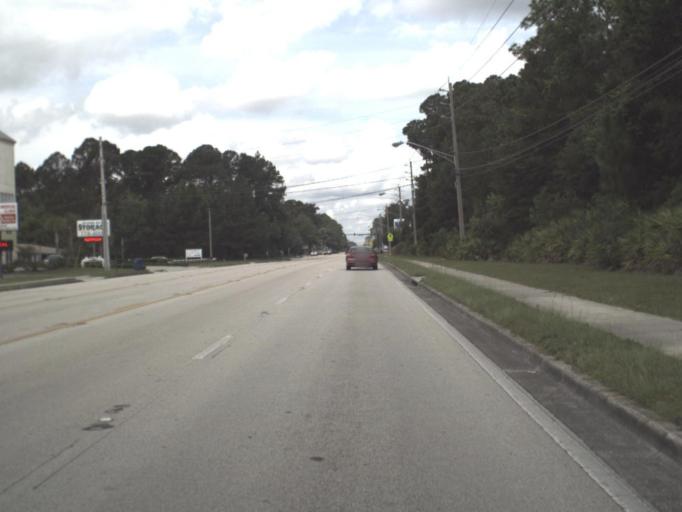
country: US
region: Florida
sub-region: Duval County
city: Jacksonville
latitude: 30.4391
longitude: -81.6798
